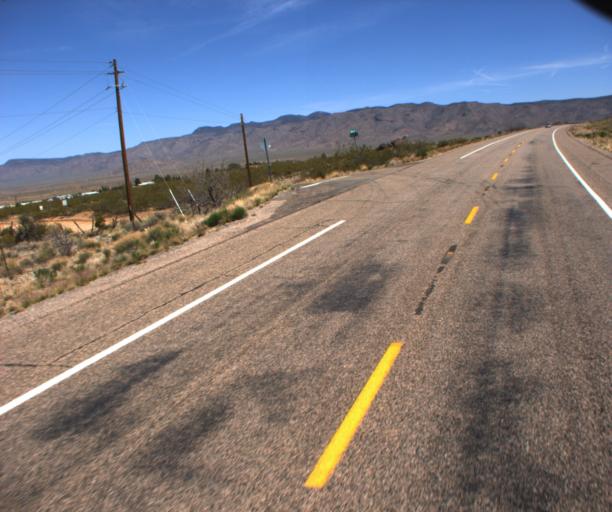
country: US
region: Arizona
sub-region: Mohave County
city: New Kingman-Butler
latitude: 35.4163
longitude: -113.8173
